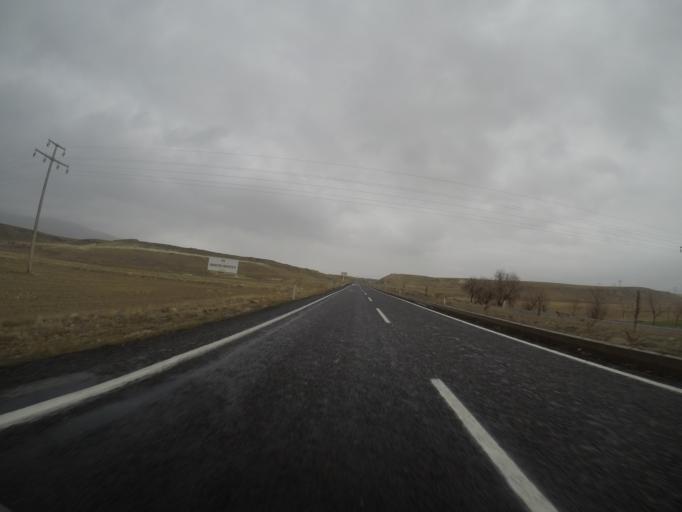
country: TR
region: Nevsehir
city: Avanos
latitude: 38.7041
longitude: 34.8707
